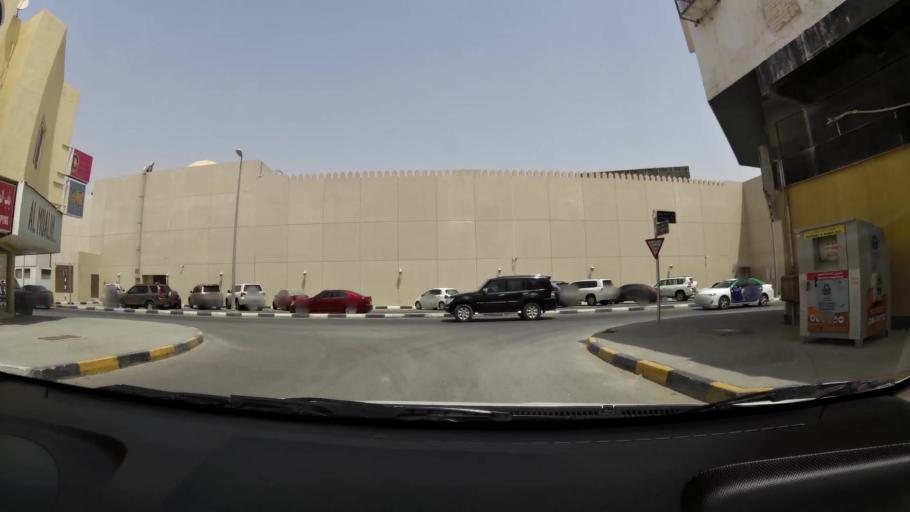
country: AE
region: Ash Shariqah
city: Sharjah
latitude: 25.3447
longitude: 55.4042
